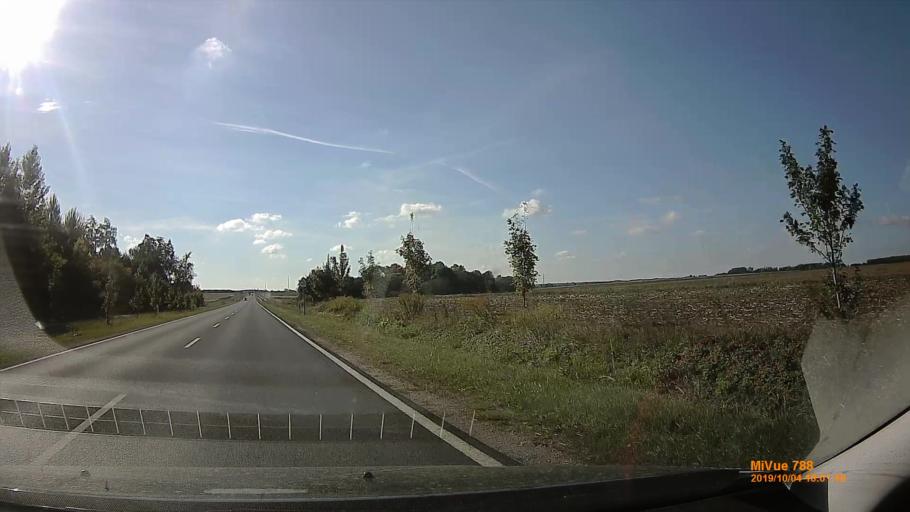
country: HU
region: Somogy
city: Kaposvar
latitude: 46.4090
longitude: 17.7716
